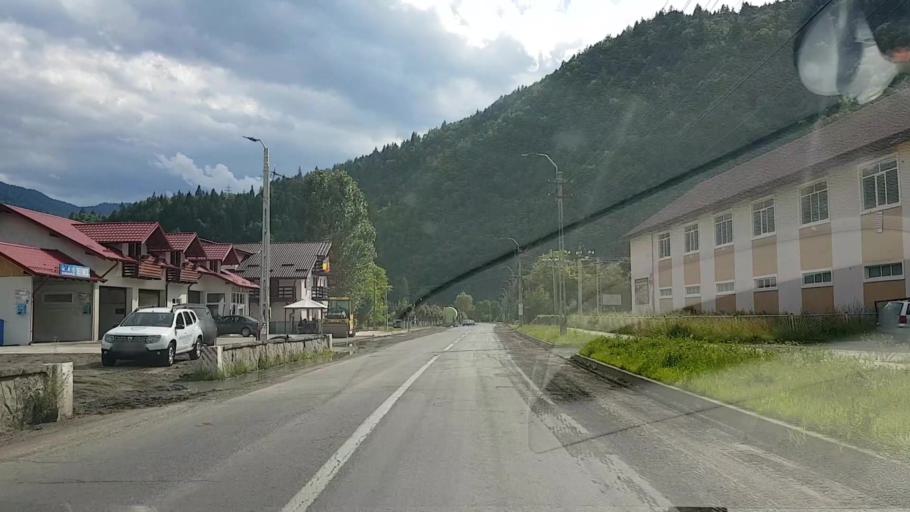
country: RO
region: Neamt
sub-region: Comuna Bicaz
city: Dodeni
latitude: 46.9211
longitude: 26.0884
